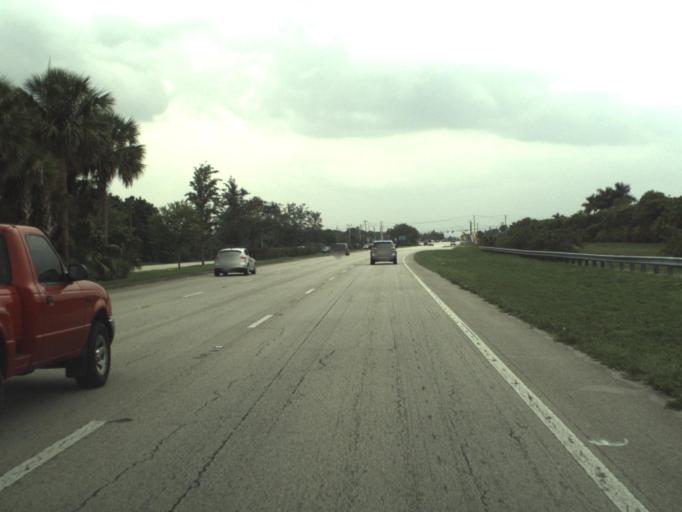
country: US
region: Florida
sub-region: Broward County
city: Southwest Ranches
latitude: 26.0694
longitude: -80.3139
